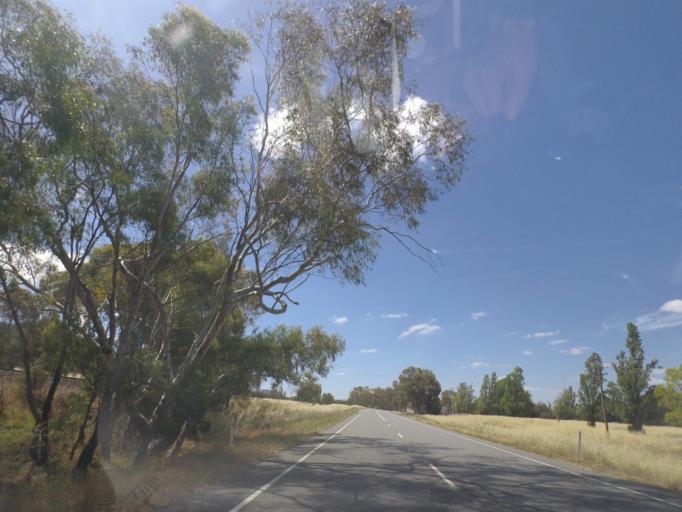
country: AU
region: Victoria
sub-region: Wangaratta
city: Wangaratta
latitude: -36.4523
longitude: 146.2378
